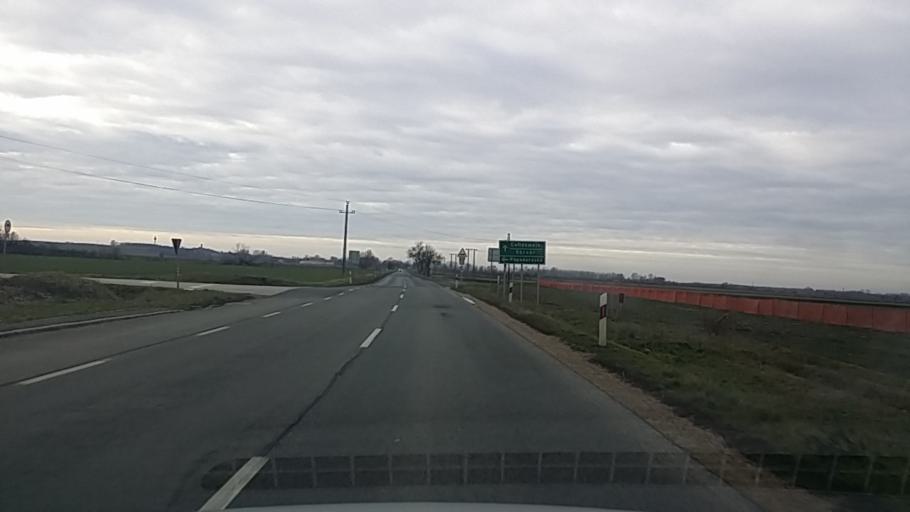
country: HU
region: Veszprem
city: Papa
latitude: 47.3008
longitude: 17.3922
